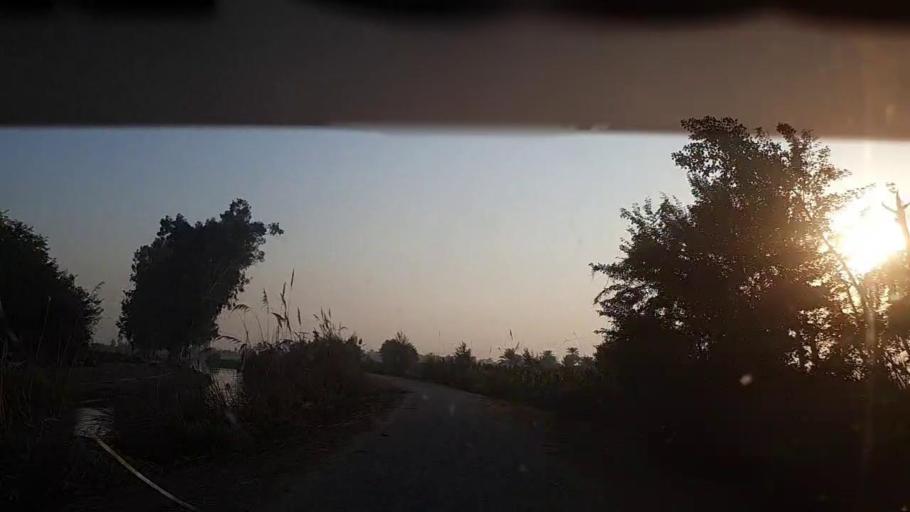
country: PK
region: Sindh
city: Ranipur
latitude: 27.2388
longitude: 68.5497
